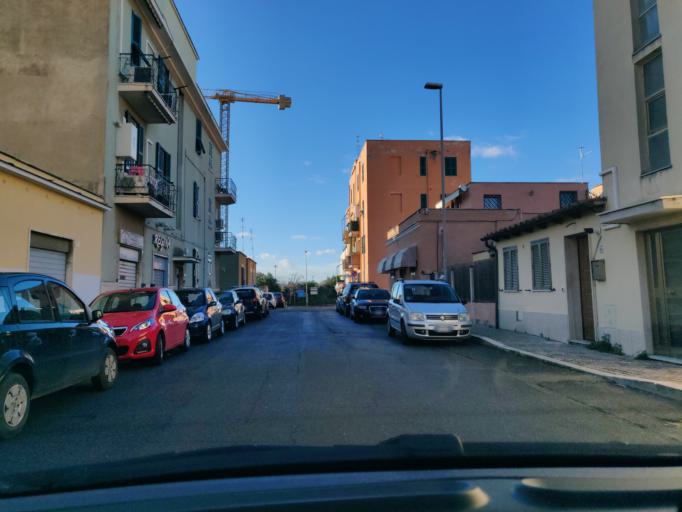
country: IT
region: Latium
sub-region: Citta metropolitana di Roma Capitale
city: Civitavecchia
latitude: 42.0995
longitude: 11.7926
